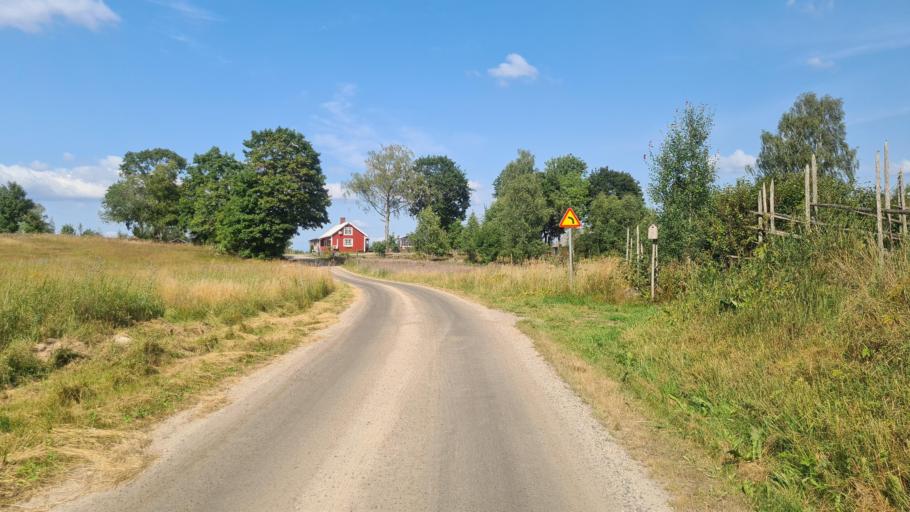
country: SE
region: Kronoberg
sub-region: Ljungby Kommun
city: Ljungby
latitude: 56.7231
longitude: 13.8860
